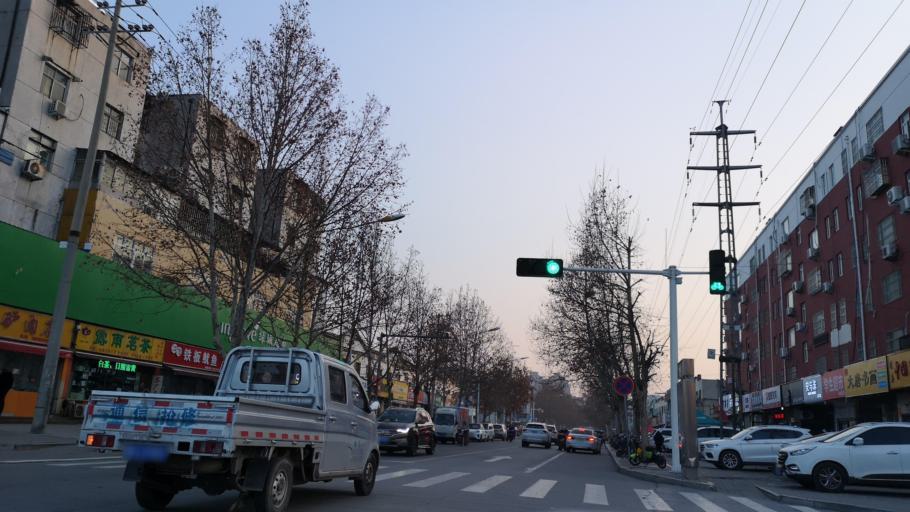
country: CN
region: Henan Sheng
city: Zhongyuanlu
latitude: 35.7681
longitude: 115.0743
